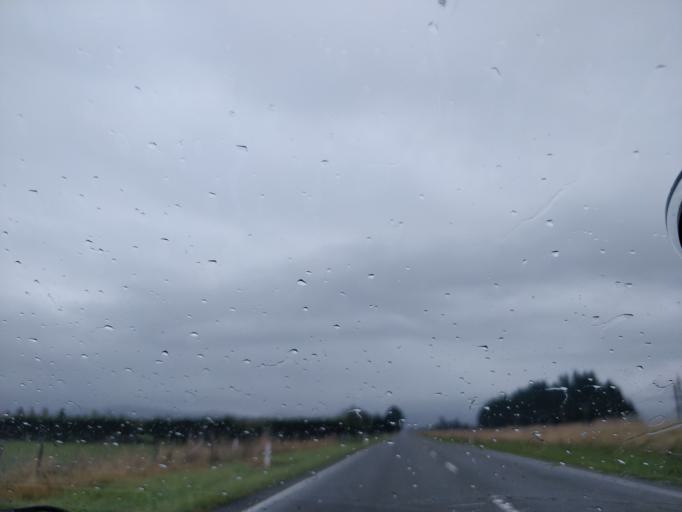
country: NZ
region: Canterbury
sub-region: Selwyn District
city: Darfield
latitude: -43.3811
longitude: 172.0058
